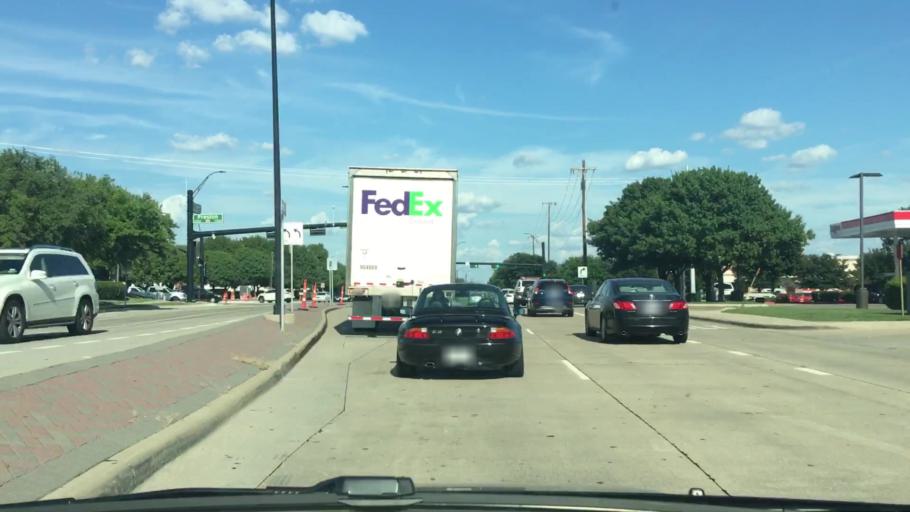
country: US
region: Texas
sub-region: Collin County
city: Frisco
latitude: 33.1390
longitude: -96.8057
